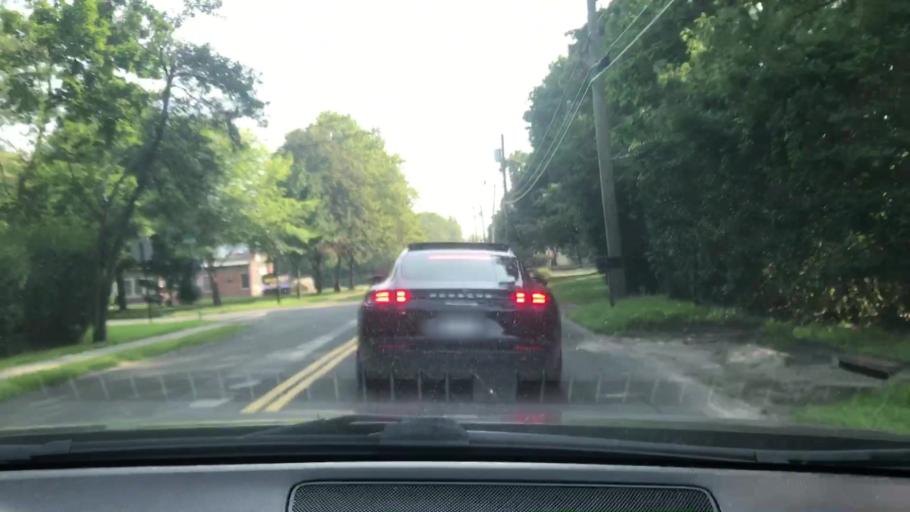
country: US
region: New York
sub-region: Suffolk County
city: Sag Harbor
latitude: 40.9897
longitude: -72.3023
